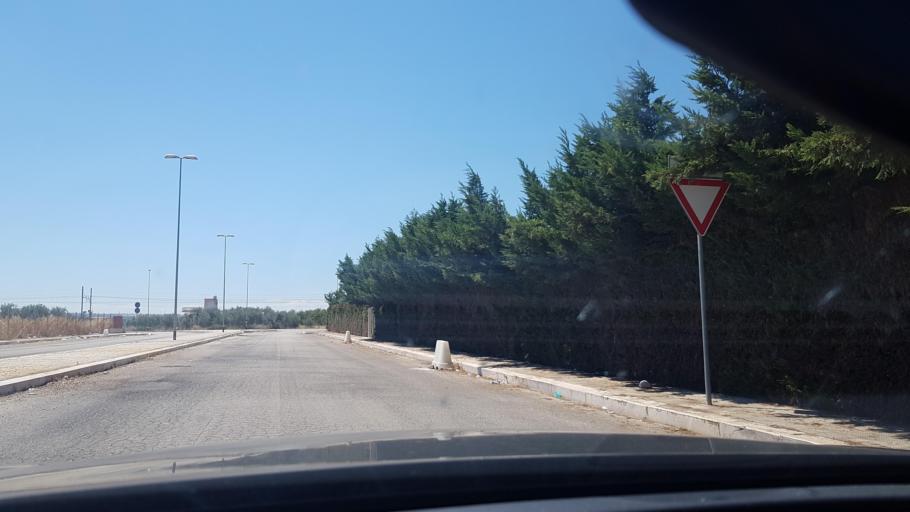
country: IT
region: Apulia
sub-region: Provincia di Barletta - Andria - Trani
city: Barletta
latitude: 41.3023
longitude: 16.3294
